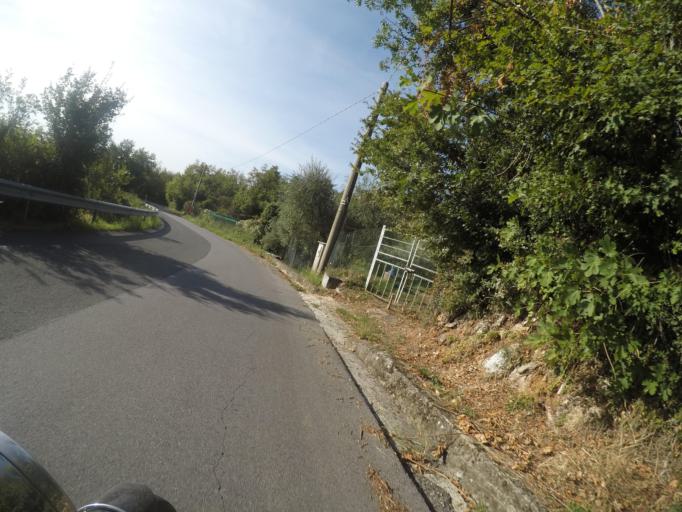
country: IT
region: Tuscany
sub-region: Provincia di Massa-Carrara
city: Massa
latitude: 44.0666
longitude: 10.1204
